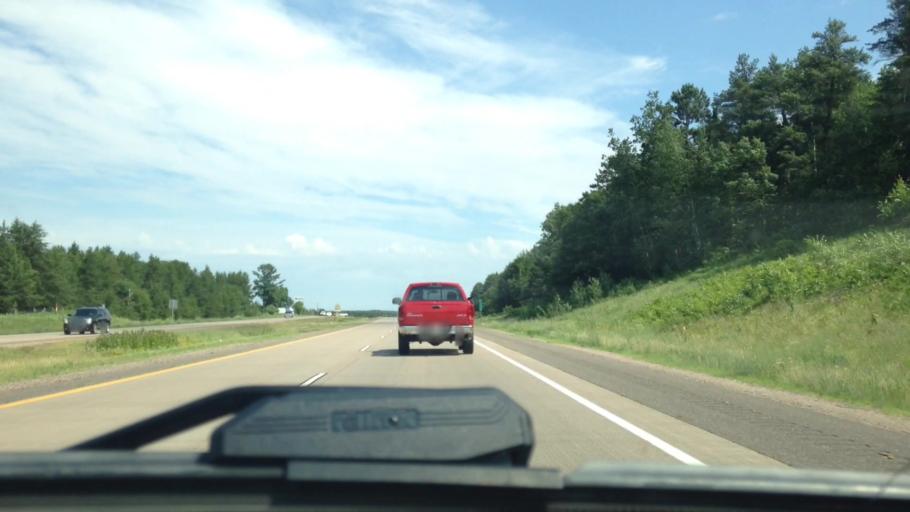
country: US
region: Wisconsin
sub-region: Washburn County
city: Spooner
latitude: 45.8937
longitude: -91.8275
